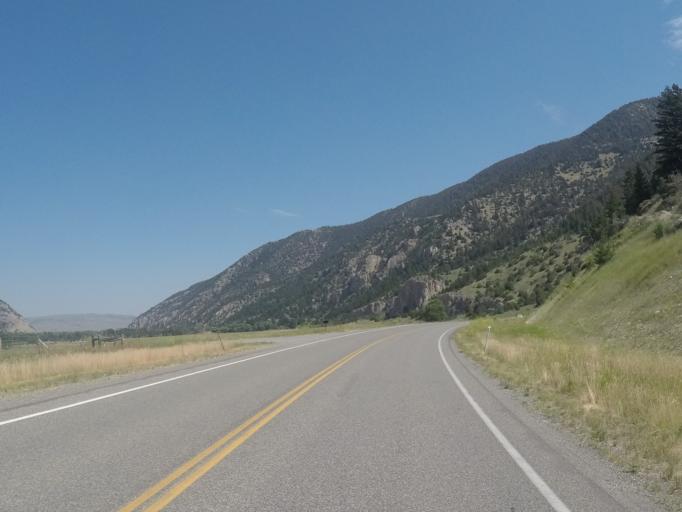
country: US
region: Montana
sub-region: Park County
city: Livingston
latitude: 45.5841
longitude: -110.5623
